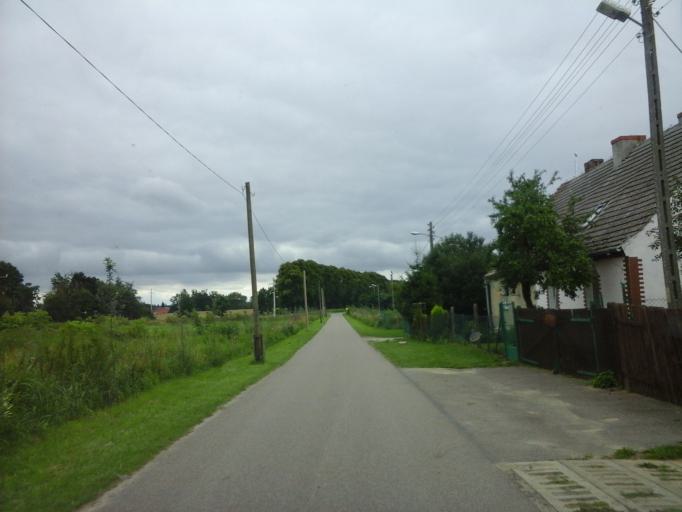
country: PL
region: West Pomeranian Voivodeship
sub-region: Powiat choszczenski
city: Pelczyce
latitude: 53.0117
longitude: 15.3889
